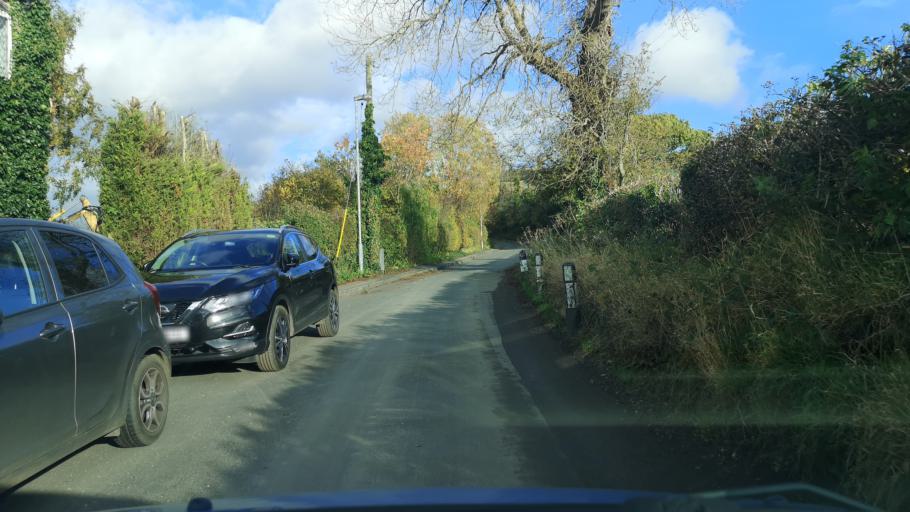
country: GB
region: England
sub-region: City and Borough of Wakefield
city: Middlestown
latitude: 53.6403
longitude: -1.6219
